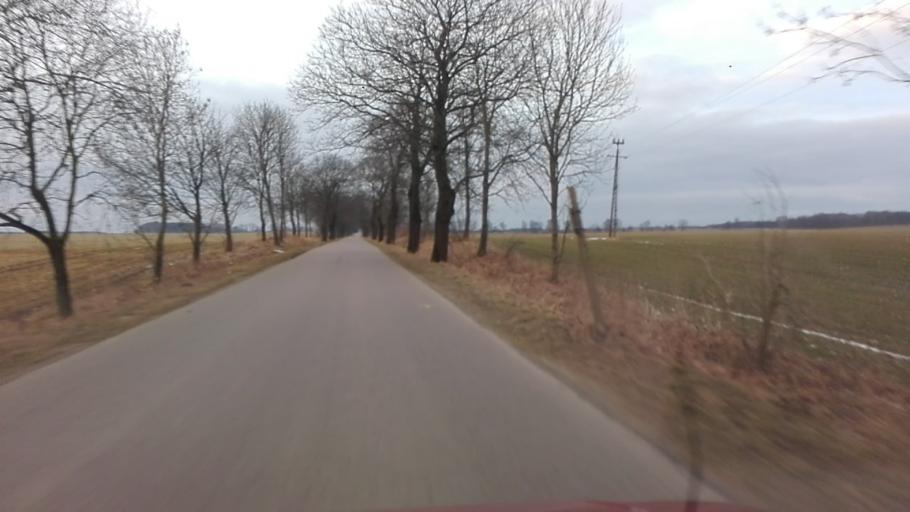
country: PL
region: West Pomeranian Voivodeship
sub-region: Powiat swidwinski
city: Rabino
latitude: 53.8065
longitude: 15.9151
